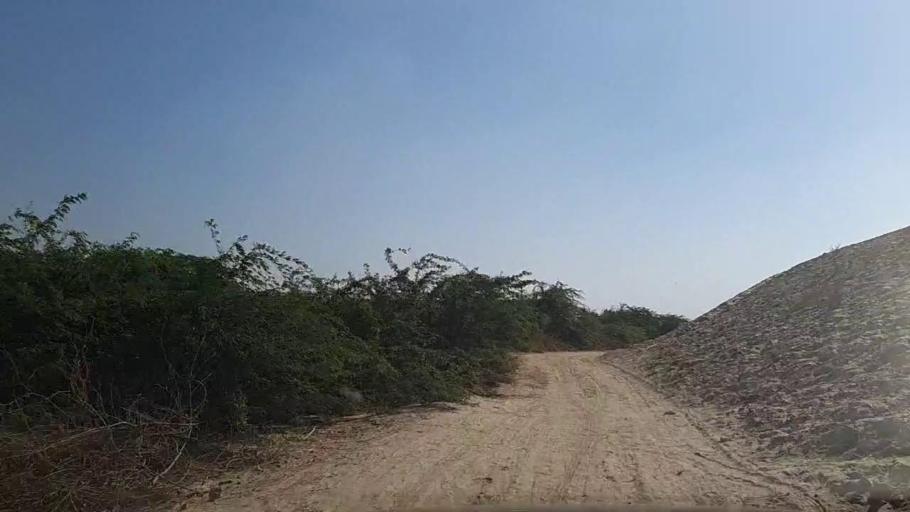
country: PK
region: Sindh
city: Daro Mehar
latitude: 24.8113
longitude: 68.0746
